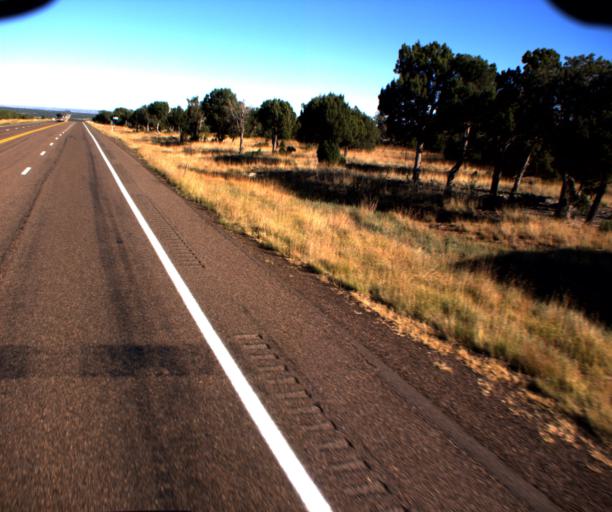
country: US
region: Arizona
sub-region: Navajo County
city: White Mountain Lake
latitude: 34.3350
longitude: -110.0485
